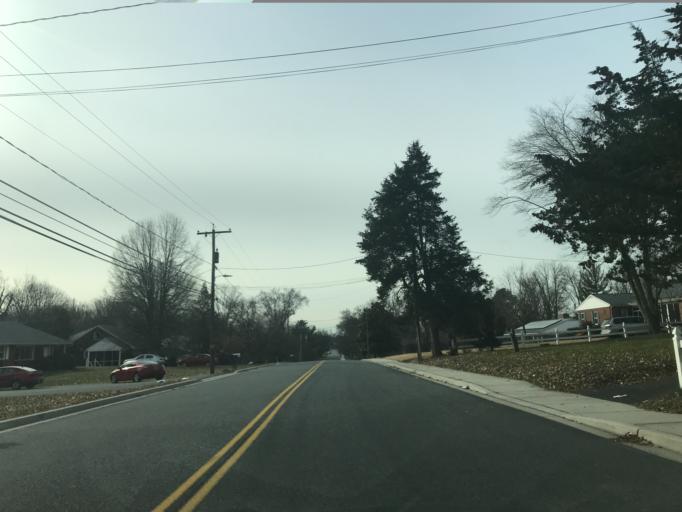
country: US
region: Maryland
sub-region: Harford County
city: Aberdeen
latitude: 39.5168
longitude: -76.1661
